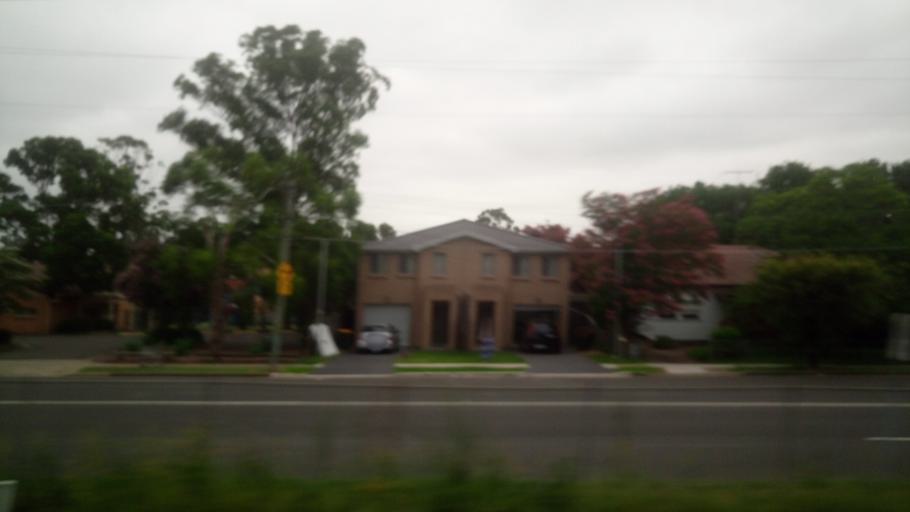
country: AU
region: New South Wales
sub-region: Blacktown
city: Mount Druitt
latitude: -33.7684
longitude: 150.8136
